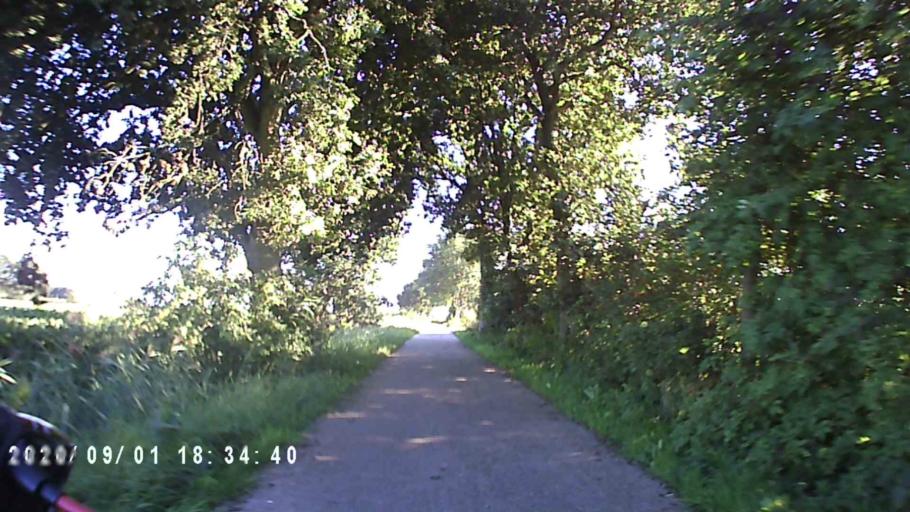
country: NL
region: Groningen
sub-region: Gemeente Hoogezand-Sappemeer
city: Sappemeer
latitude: 53.1506
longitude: 6.8030
